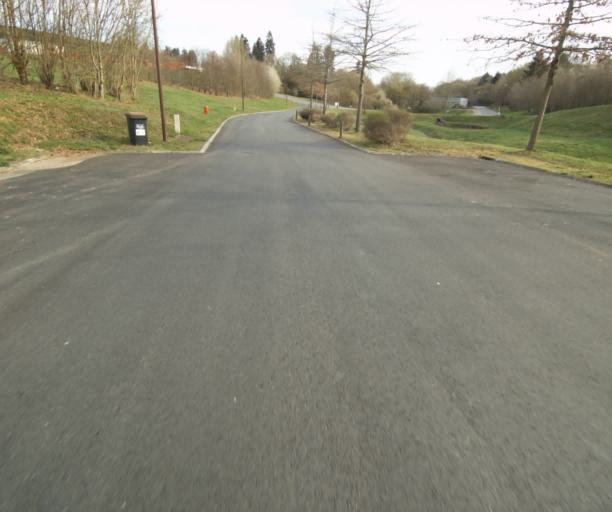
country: FR
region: Limousin
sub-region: Departement de la Correze
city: Naves
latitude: 45.3248
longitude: 1.7659
